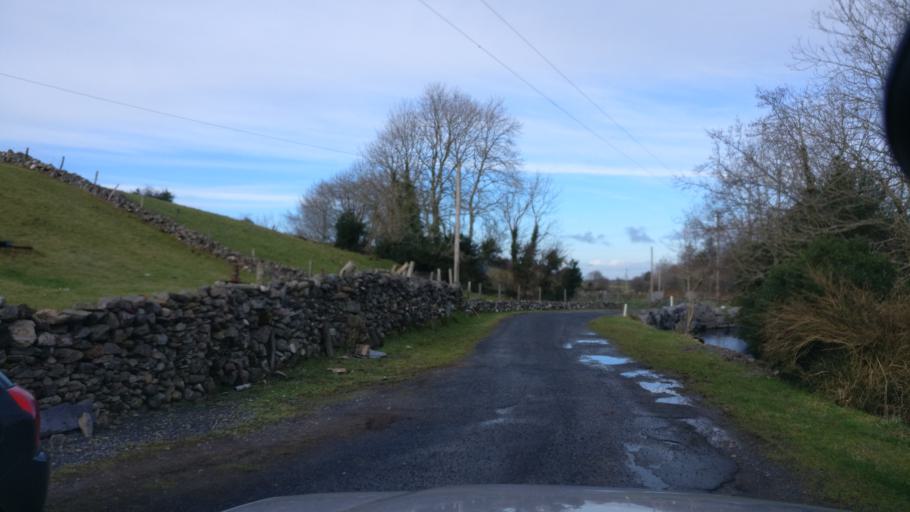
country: IE
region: Connaught
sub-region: County Galway
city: Oughterard
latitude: 53.5527
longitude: -9.4484
